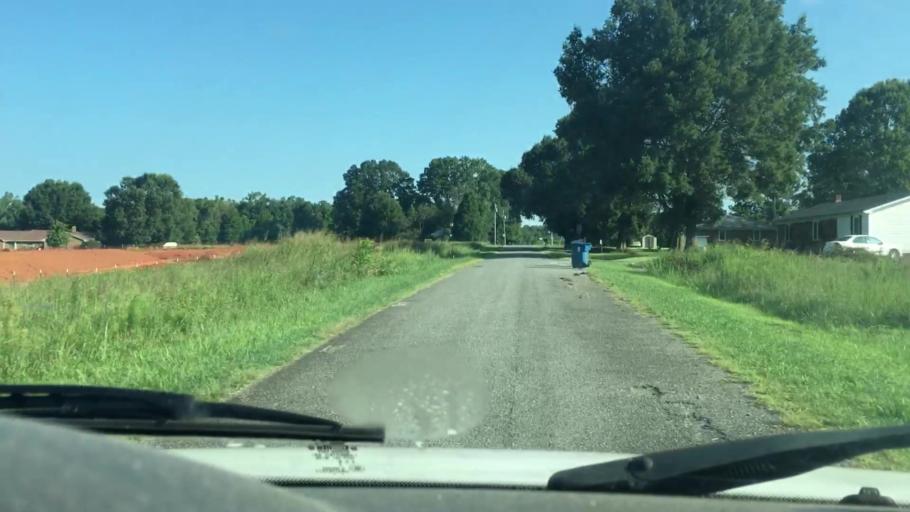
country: US
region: North Carolina
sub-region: Mecklenburg County
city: Huntersville
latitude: 35.4264
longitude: -80.8087
